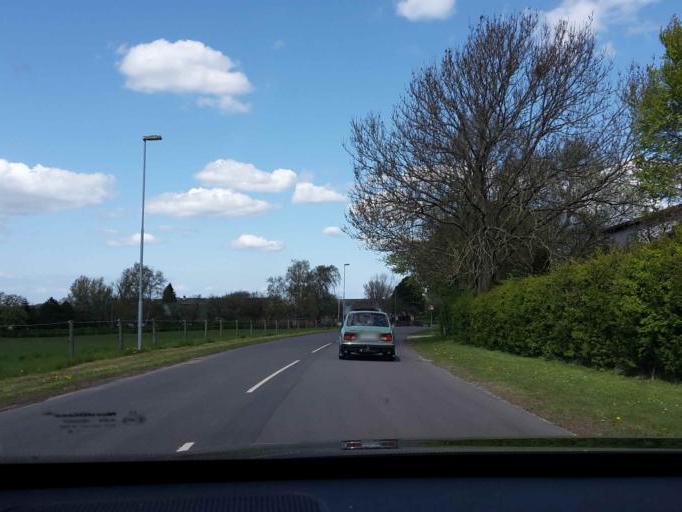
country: DK
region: South Denmark
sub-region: Odense Kommune
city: Bellinge
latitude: 55.3976
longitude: 10.3068
